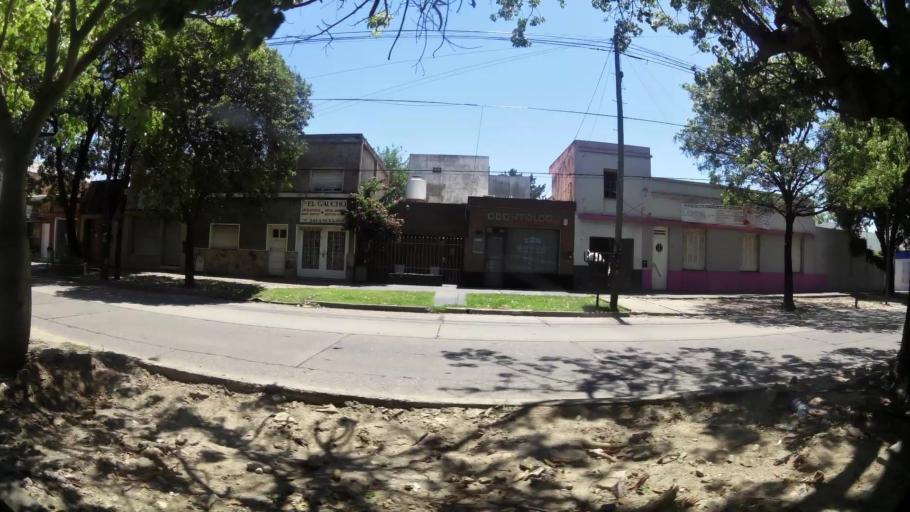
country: AR
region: Cordoba
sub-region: Departamento de Capital
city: Cordoba
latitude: -31.4091
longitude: -64.2174
